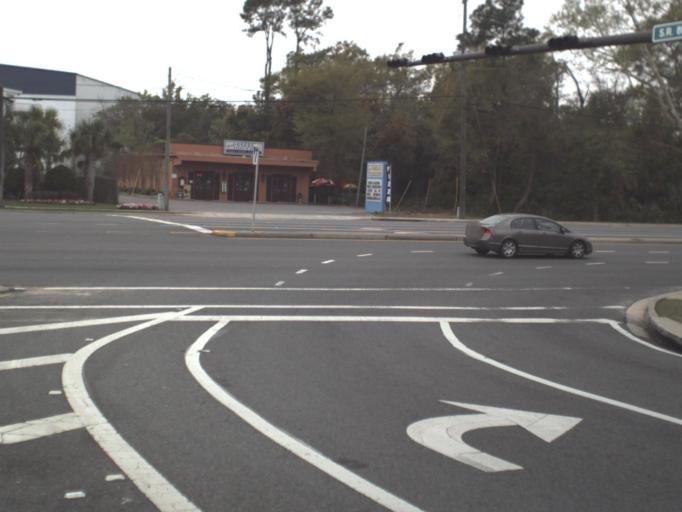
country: US
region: Florida
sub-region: Okaloosa County
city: Niceville
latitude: 30.5226
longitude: -86.4937
